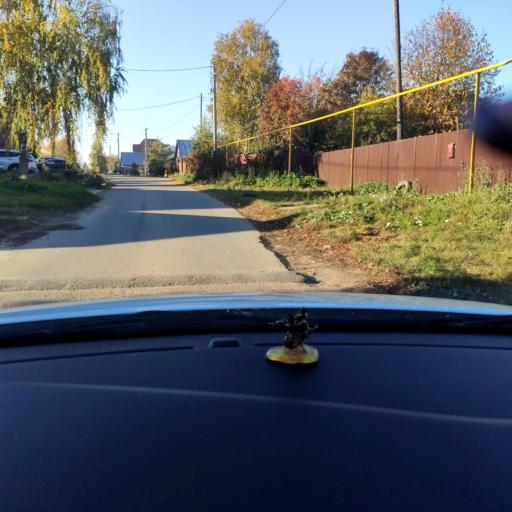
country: RU
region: Tatarstan
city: Stolbishchi
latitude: 55.6243
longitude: 49.1536
